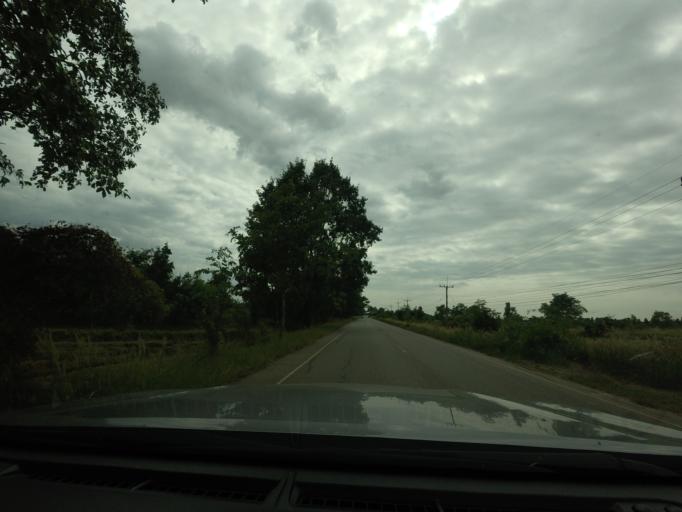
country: TH
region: Phitsanulok
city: Noen Maprang
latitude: 16.6585
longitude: 100.6155
